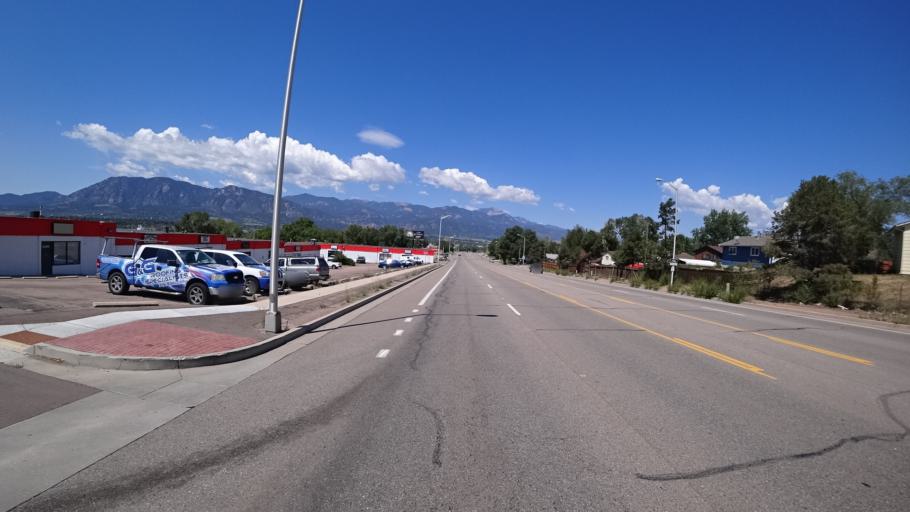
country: US
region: Colorado
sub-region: El Paso County
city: Stratmoor
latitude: 38.7964
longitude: -104.7731
